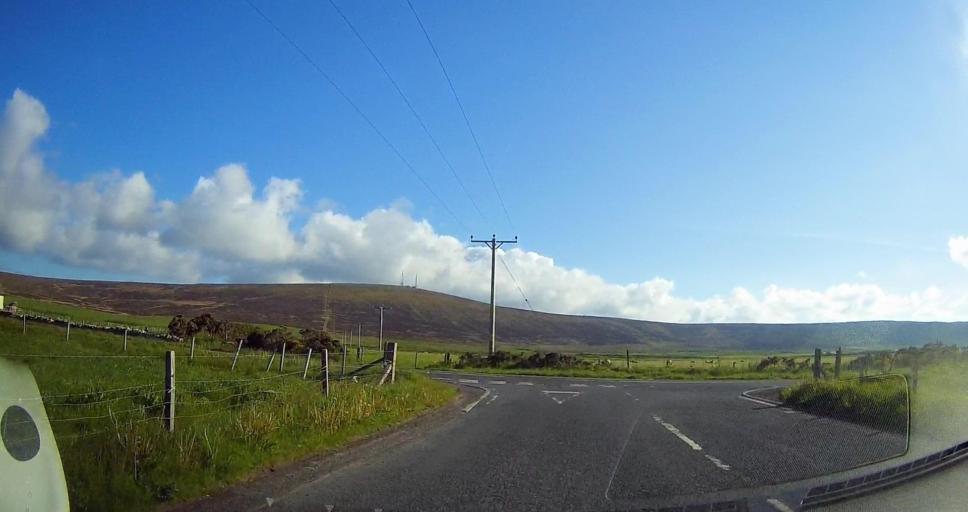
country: GB
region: Scotland
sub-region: Orkney Islands
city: Orkney
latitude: 58.9924
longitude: -3.0730
